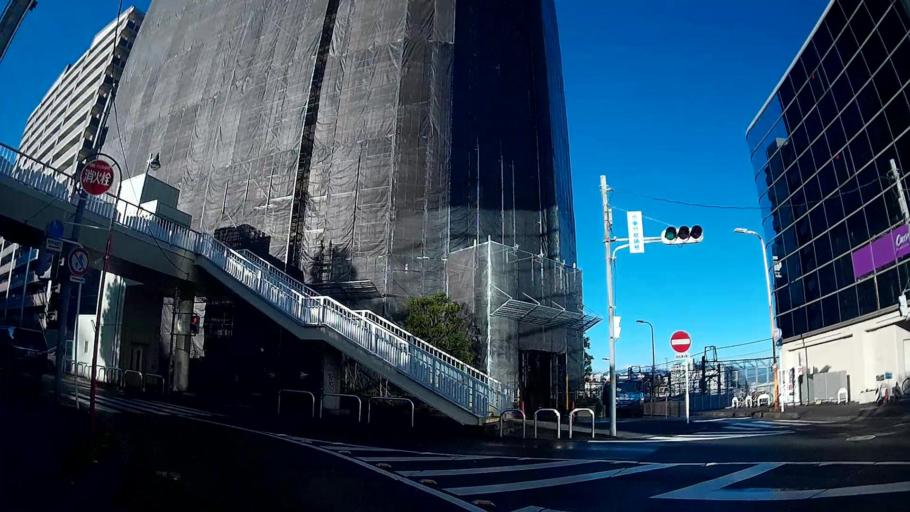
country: JP
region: Saitama
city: Sayama
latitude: 35.8410
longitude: 139.3888
